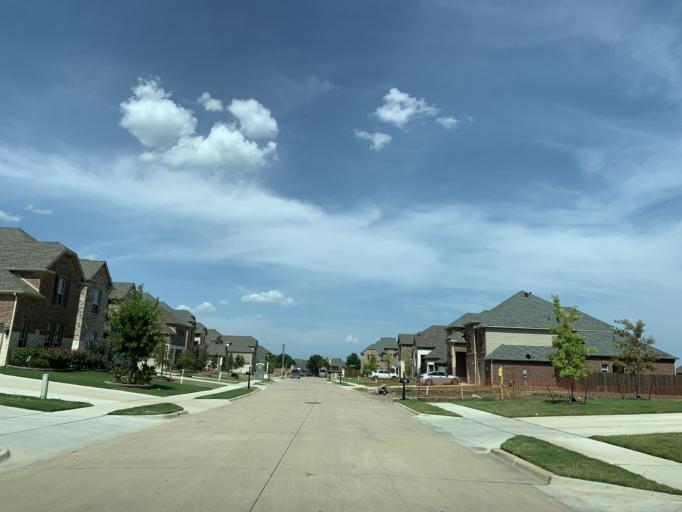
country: US
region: Texas
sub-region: Dallas County
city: Cedar Hill
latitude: 32.6467
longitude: -97.0089
